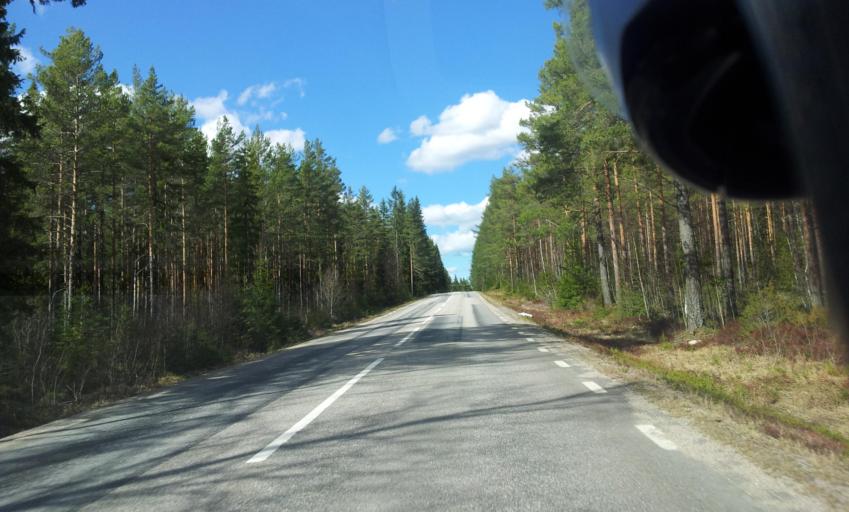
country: SE
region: Gaevleborg
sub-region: Ovanakers Kommun
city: Edsbyn
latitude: 61.3455
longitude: 15.8186
